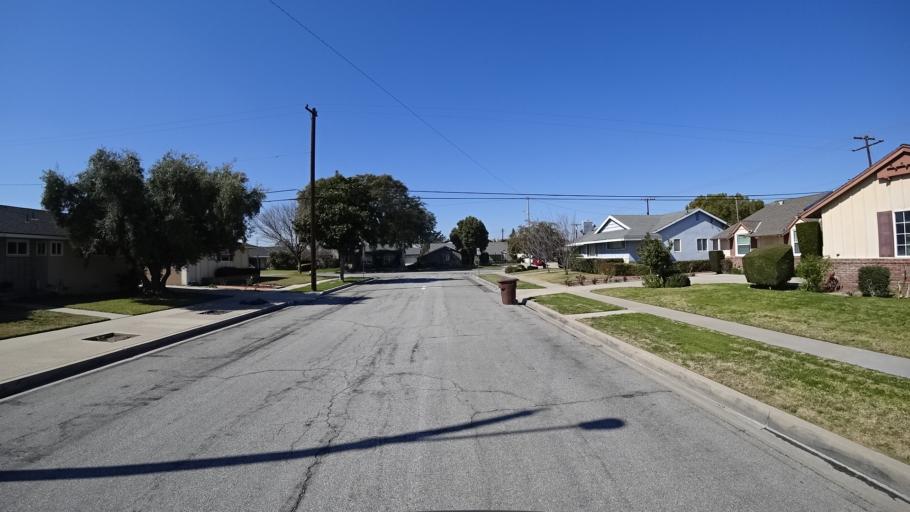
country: US
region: California
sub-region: Orange County
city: Anaheim
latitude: 33.8098
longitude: -117.9343
